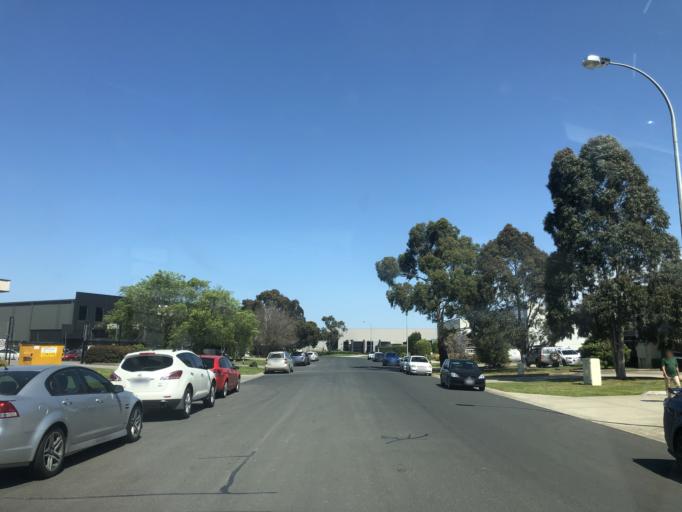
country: AU
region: Victoria
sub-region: Casey
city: Hampton Park
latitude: -38.0260
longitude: 145.2309
